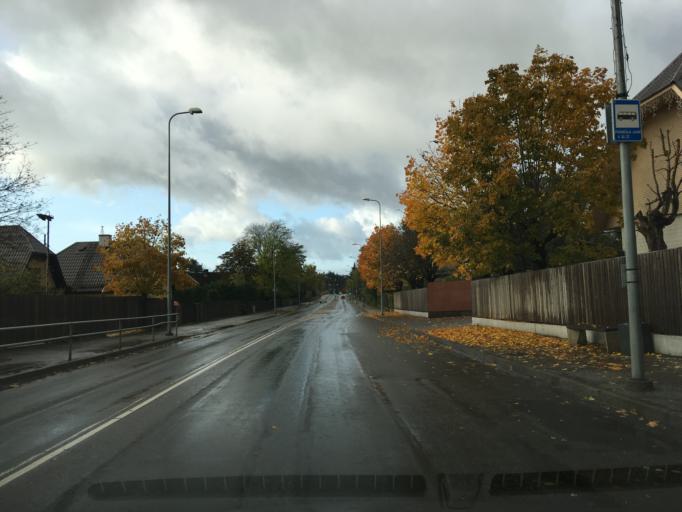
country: EE
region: Harju
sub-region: Saue vald
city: Laagri
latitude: 59.3688
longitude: 24.6372
